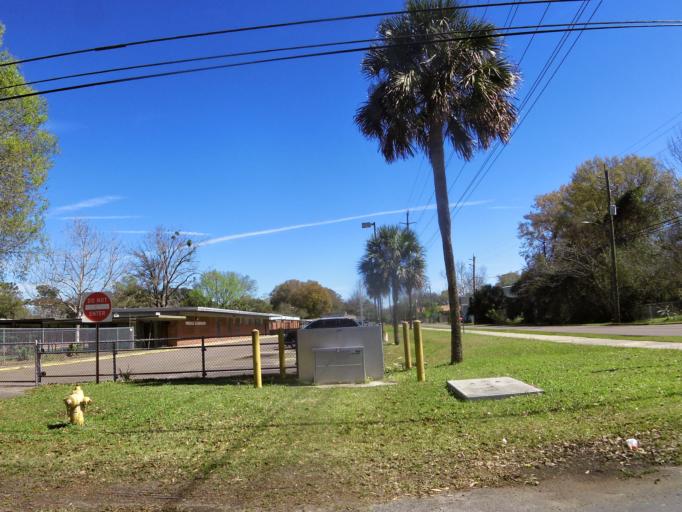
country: US
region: Florida
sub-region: Duval County
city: Jacksonville
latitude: 30.3226
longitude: -81.7224
